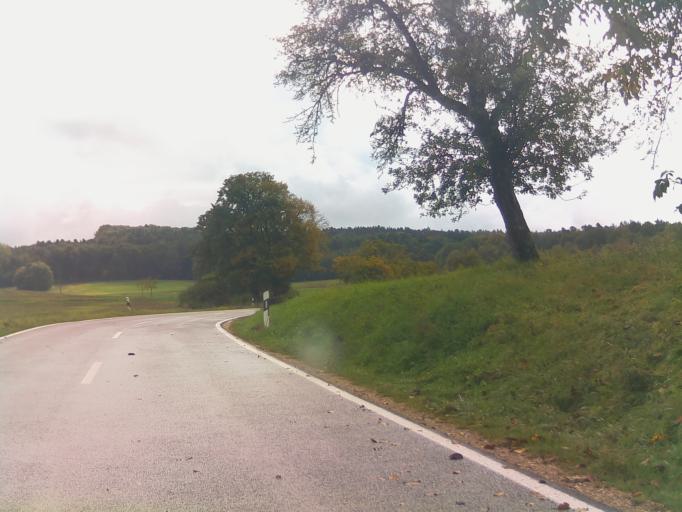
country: DE
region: Bavaria
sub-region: Upper Franconia
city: Zapfendorf
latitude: 50.0124
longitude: 10.9765
